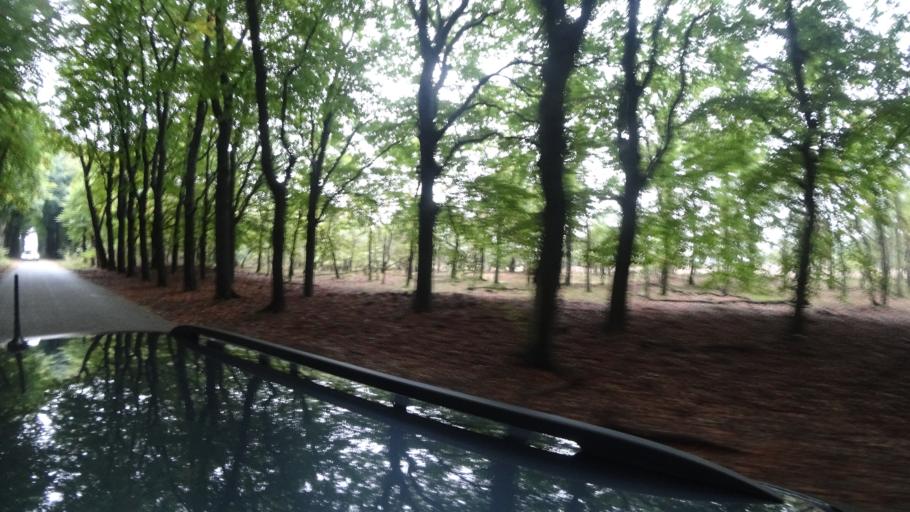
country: NL
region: Gelderland
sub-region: Gemeente Renkum
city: Heelsum
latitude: 52.0408
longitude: 5.7300
